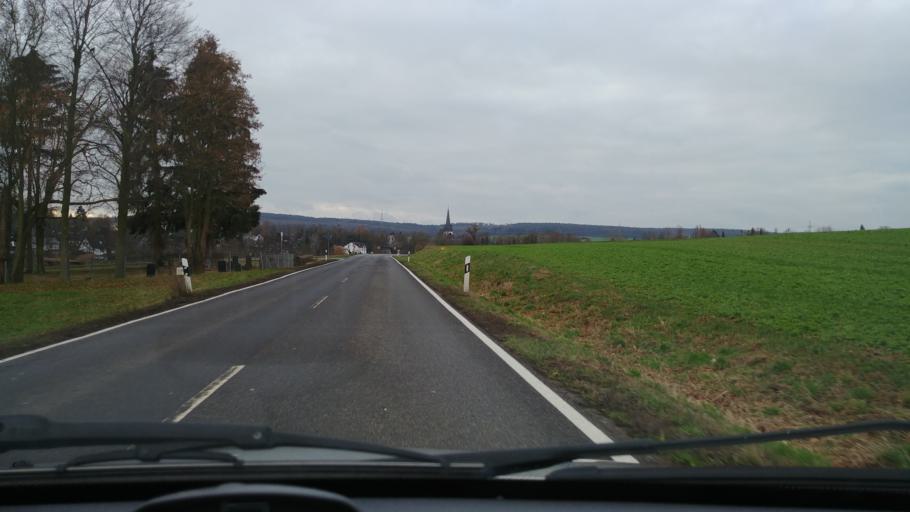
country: DE
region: Rheinland-Pfalz
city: Netzbach
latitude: 50.3162
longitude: 8.1628
